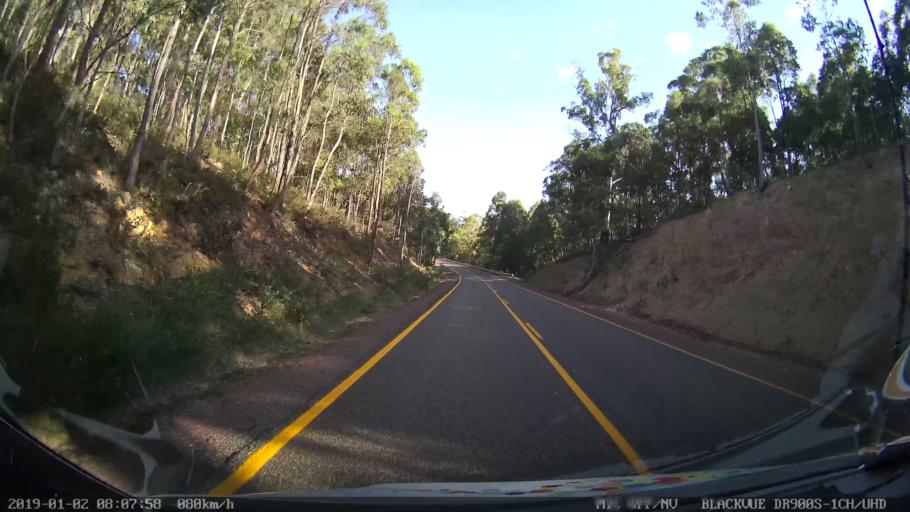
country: AU
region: New South Wales
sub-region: Tumut Shire
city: Tumut
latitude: -35.6211
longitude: 148.3886
